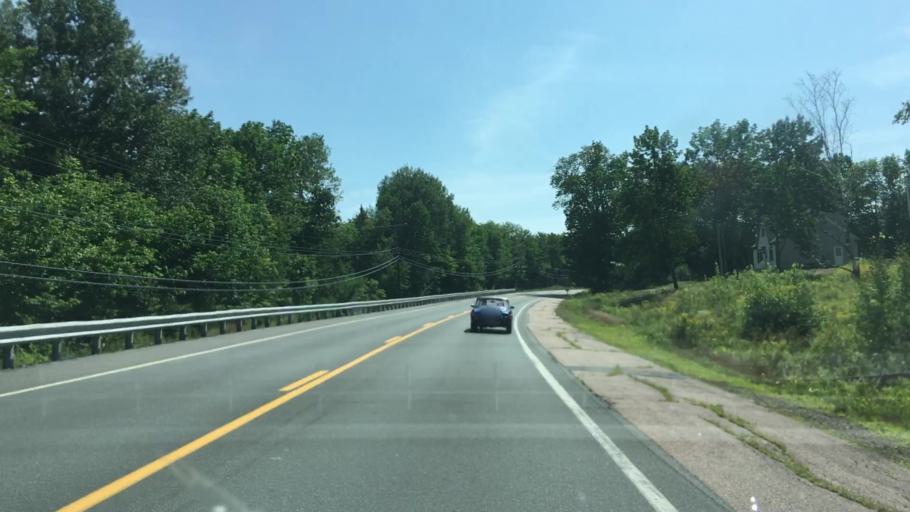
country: US
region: Maine
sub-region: Washington County
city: Calais
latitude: 45.1618
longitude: -67.1950
